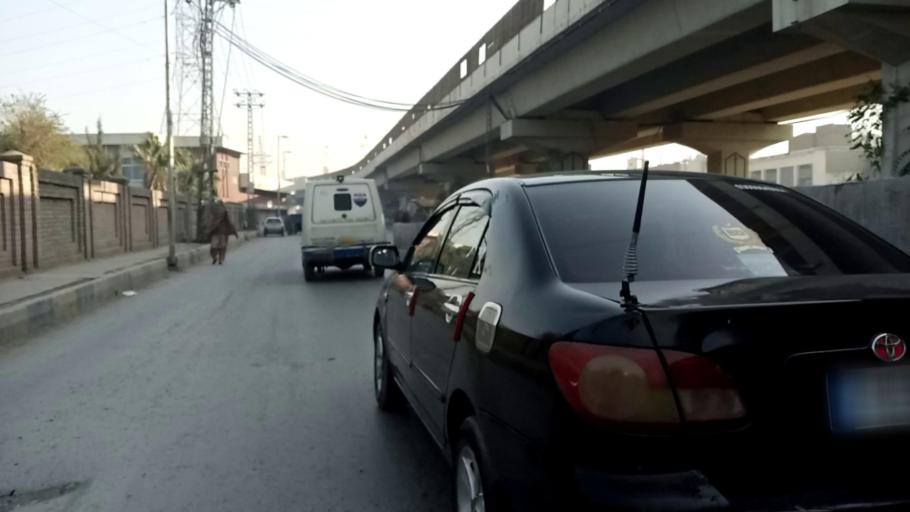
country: PK
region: Khyber Pakhtunkhwa
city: Peshawar
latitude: 34.0163
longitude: 71.5696
